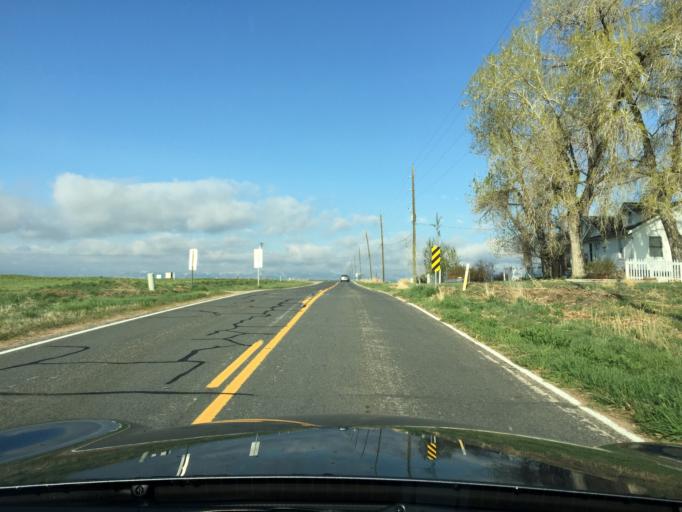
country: US
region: Colorado
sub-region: Boulder County
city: Longmont
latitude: 40.1173
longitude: -105.0821
